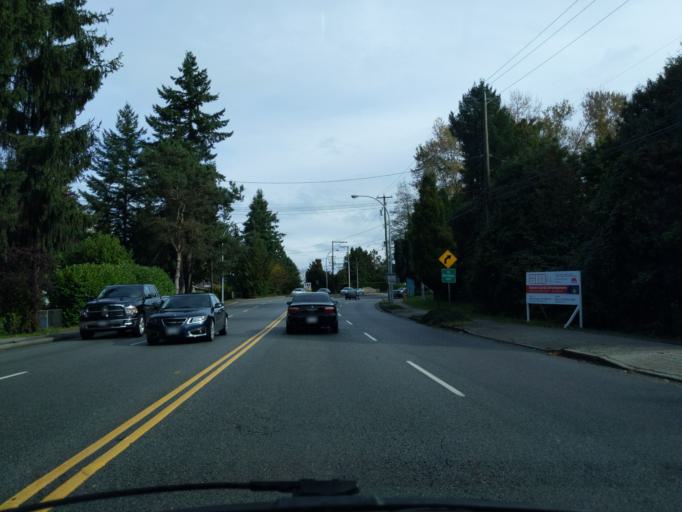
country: CA
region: British Columbia
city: Surrey
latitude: 49.1987
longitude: -122.8057
